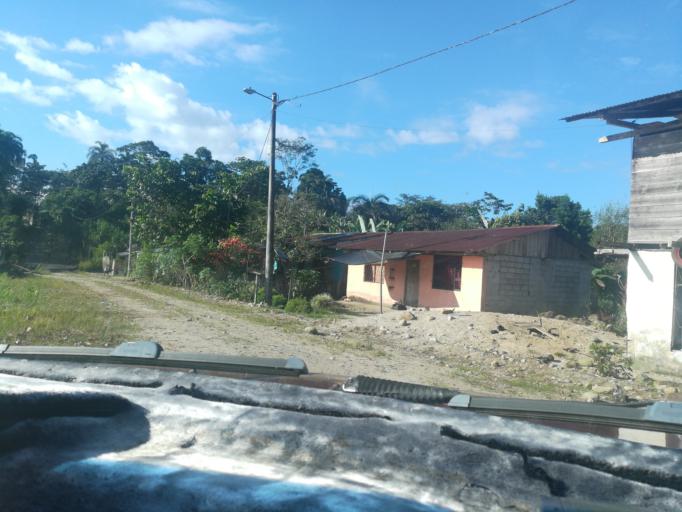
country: EC
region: Napo
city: Tena
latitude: -0.9921
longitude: -77.8337
